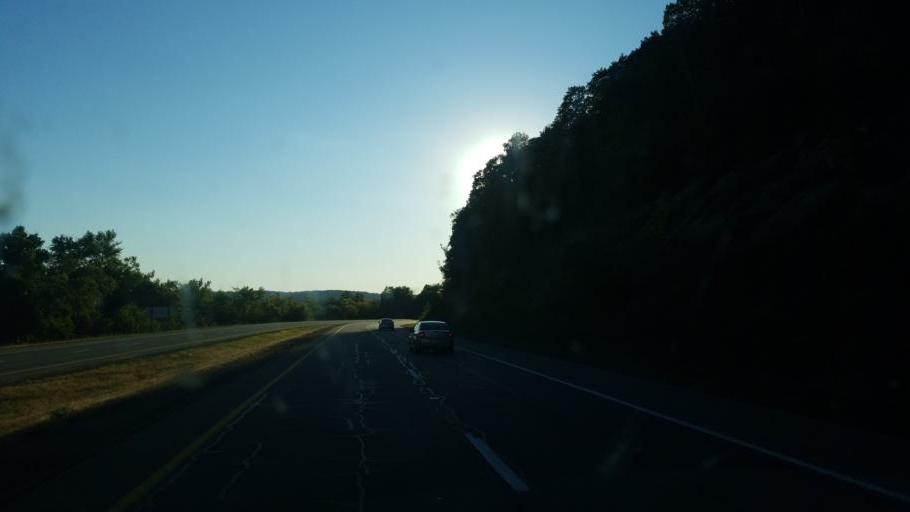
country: US
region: Ohio
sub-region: Coshocton County
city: West Lafayette
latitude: 40.2887
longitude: -81.7223
